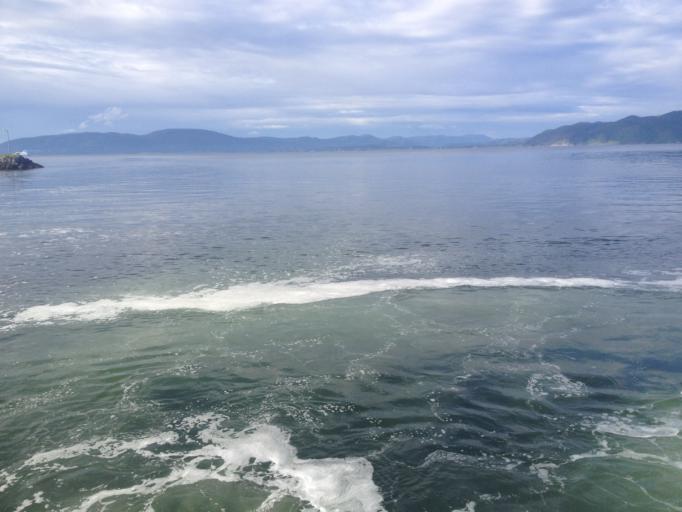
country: NO
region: Sor-Trondelag
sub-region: Agdenes
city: Lensvik
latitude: 63.5050
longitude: 9.8317
